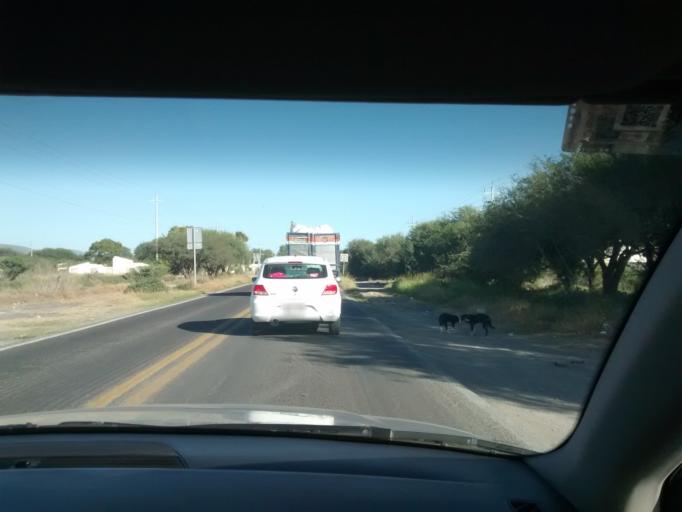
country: MX
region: Puebla
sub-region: Tehuacan
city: Magdalena Cuayucatepec
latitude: 18.5201
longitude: -97.5059
